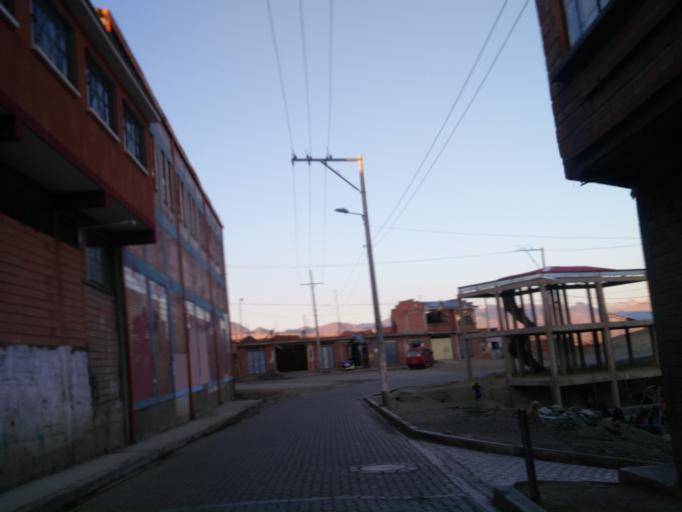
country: BO
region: La Paz
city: La Paz
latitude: -16.4797
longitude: -68.1656
